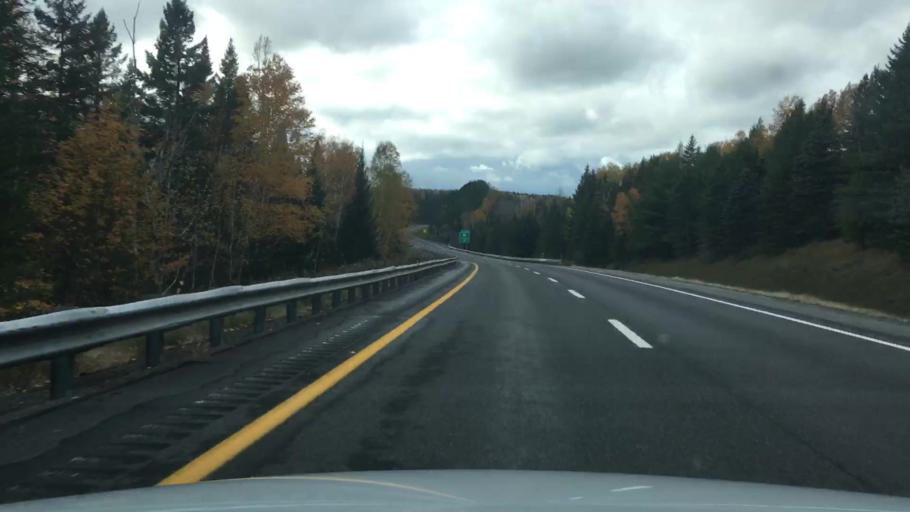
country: US
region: Maine
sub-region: Aroostook County
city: Hodgdon
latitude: 46.1453
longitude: -68.0518
